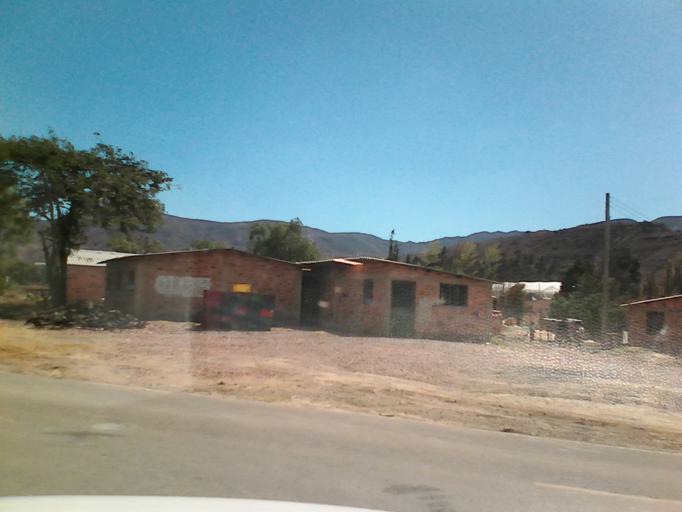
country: CO
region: Boyaca
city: Sachica
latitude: 5.6052
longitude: -73.5581
